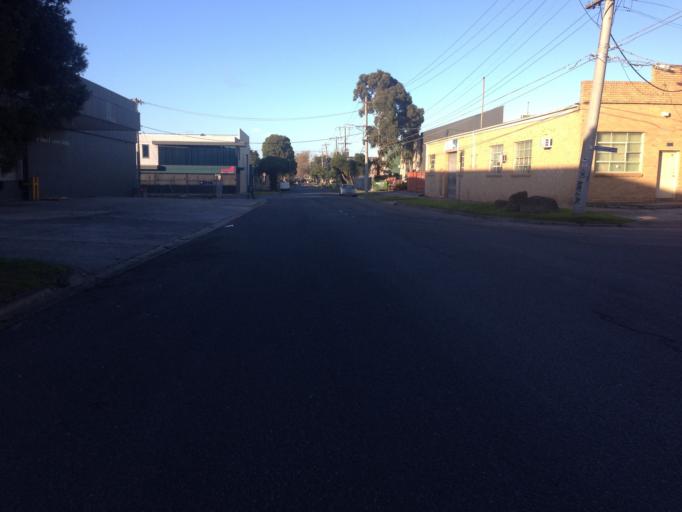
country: AU
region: Victoria
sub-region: Darebin
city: Fairfield
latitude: -37.7682
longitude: 145.0283
